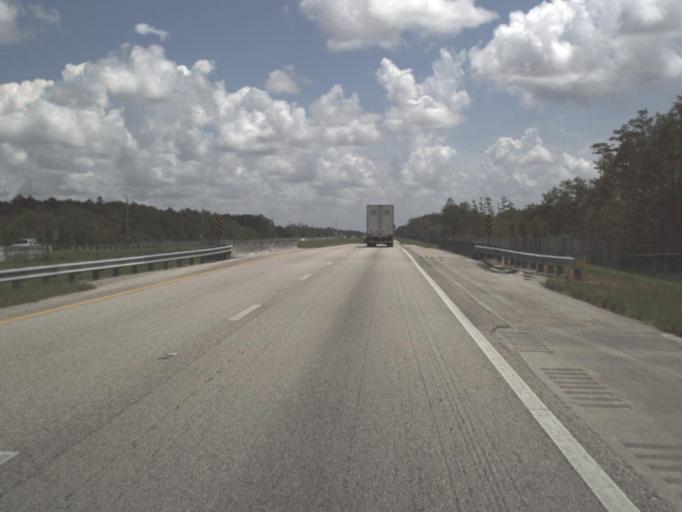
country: US
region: Florida
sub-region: Collier County
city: Immokalee
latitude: 26.1661
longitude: -81.2357
